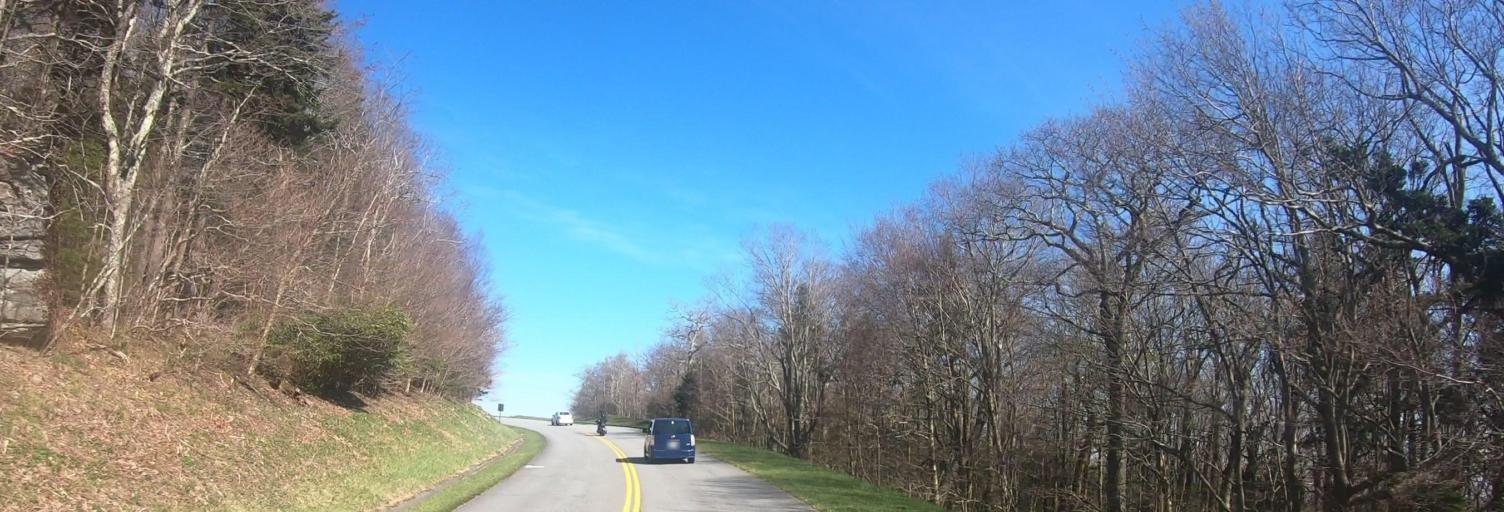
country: US
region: North Carolina
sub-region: Watauga County
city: Foscoe
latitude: 36.0973
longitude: -81.7865
